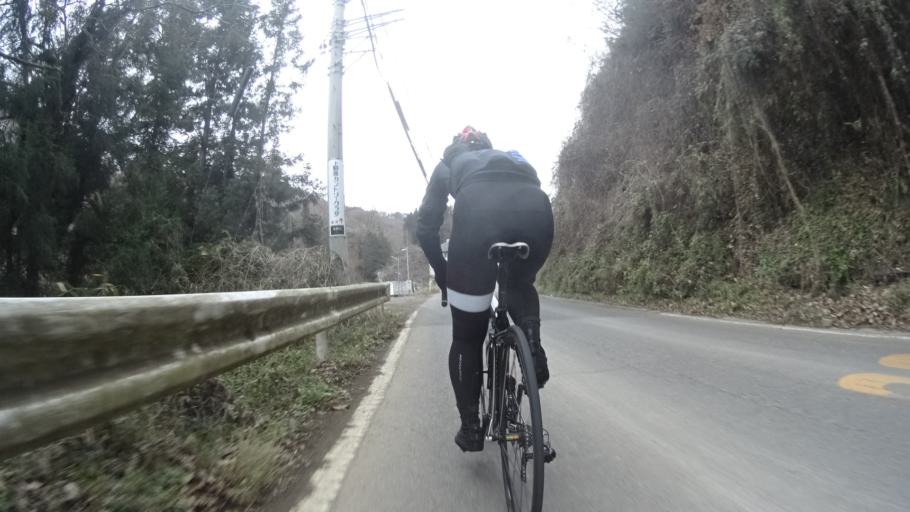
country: JP
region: Yamanashi
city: Uenohara
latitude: 35.6338
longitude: 139.1244
